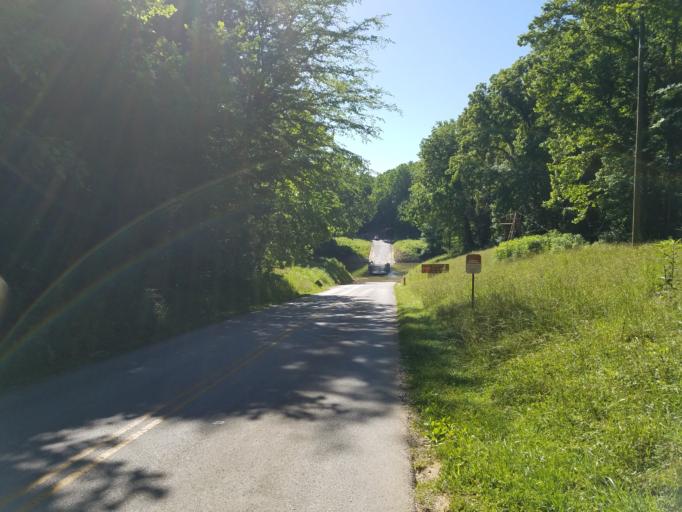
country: US
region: Kentucky
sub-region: Edmonson County
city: Brownsville
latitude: 37.1801
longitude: -86.1144
